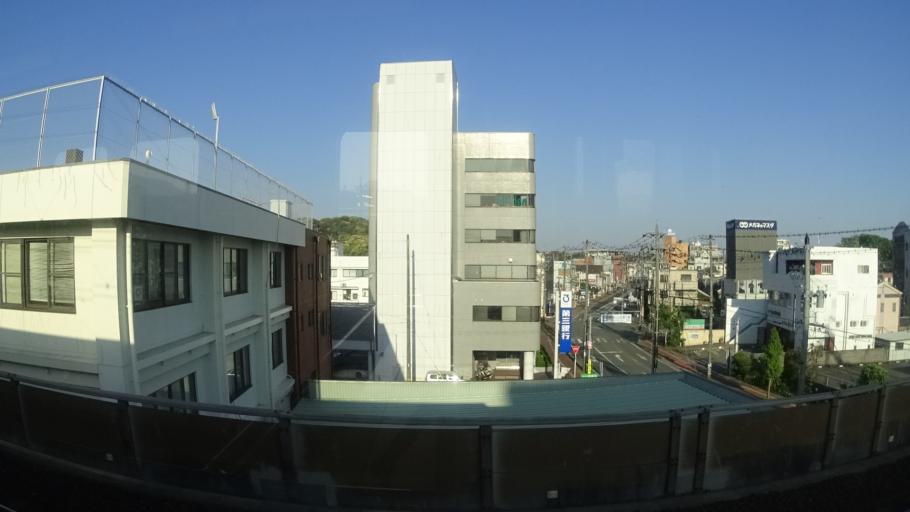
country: JP
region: Mie
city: Ise
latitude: 34.4866
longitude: 136.7139
